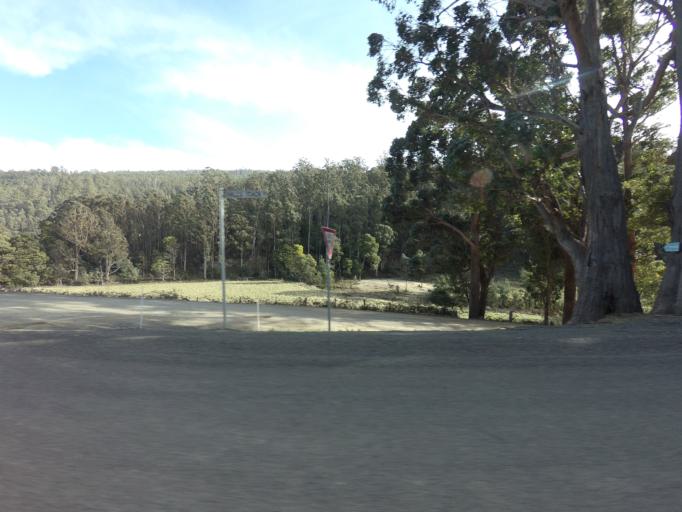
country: AU
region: Tasmania
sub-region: Huon Valley
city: Huonville
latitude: -43.0448
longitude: 147.1169
